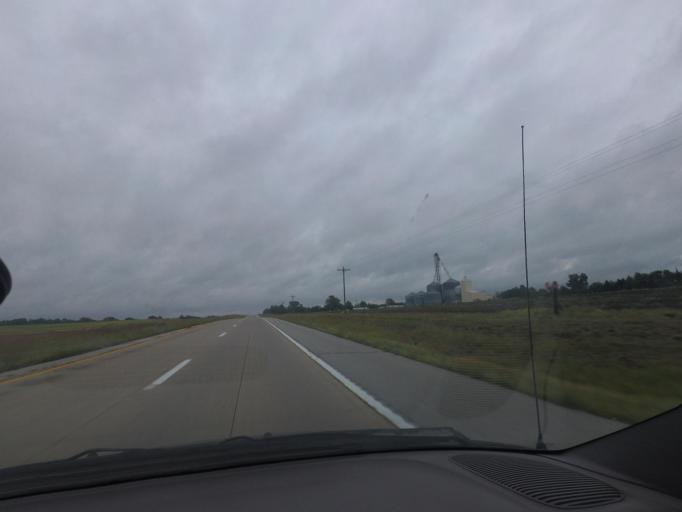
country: US
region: Missouri
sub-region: Marion County
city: Monroe City
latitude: 39.6583
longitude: -91.7995
